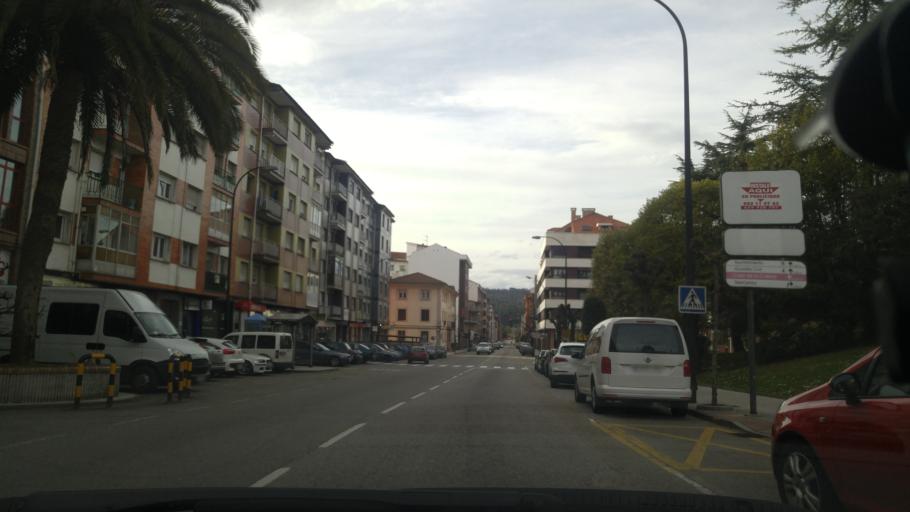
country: ES
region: Asturias
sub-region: Province of Asturias
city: Llanera
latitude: 43.4389
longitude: -5.8504
